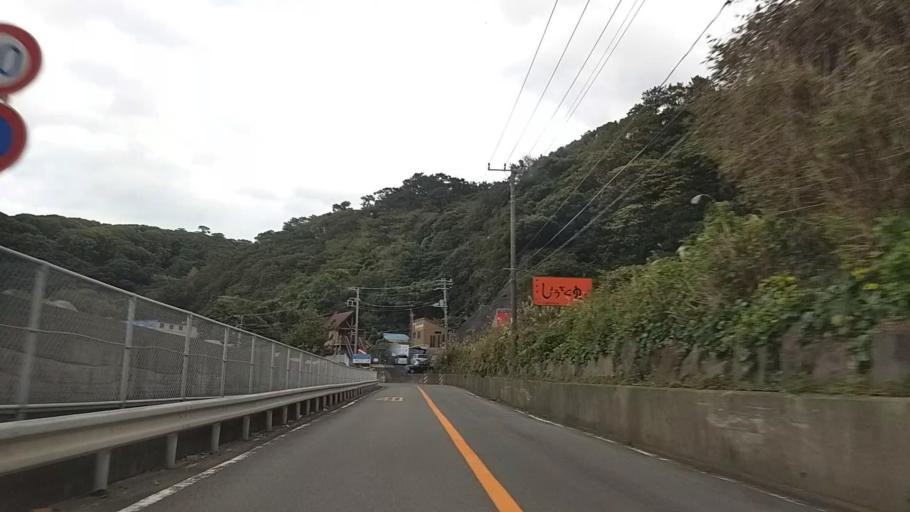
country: JP
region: Kanagawa
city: Yugawara
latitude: 35.1474
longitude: 139.1494
